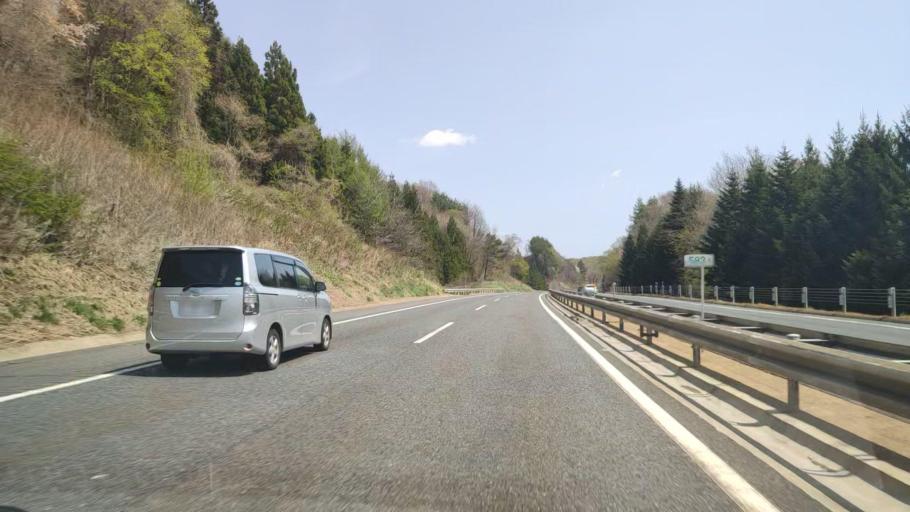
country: JP
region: Iwate
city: Ichinohe
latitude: 40.2144
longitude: 141.2232
